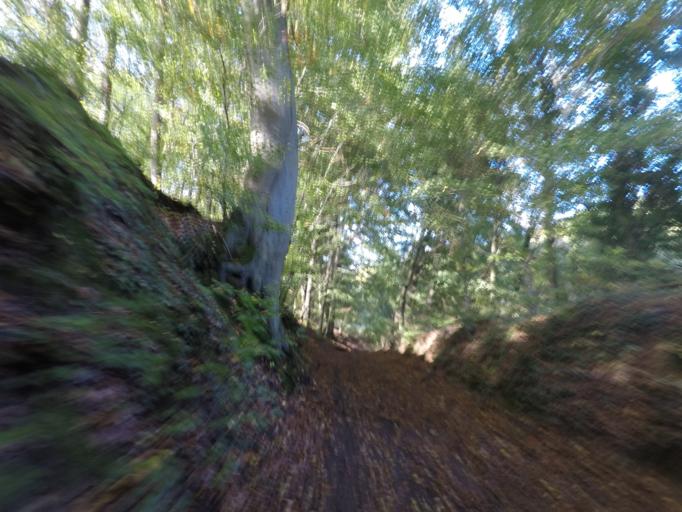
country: LU
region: Luxembourg
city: Itzig
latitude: 49.5934
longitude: 6.1740
